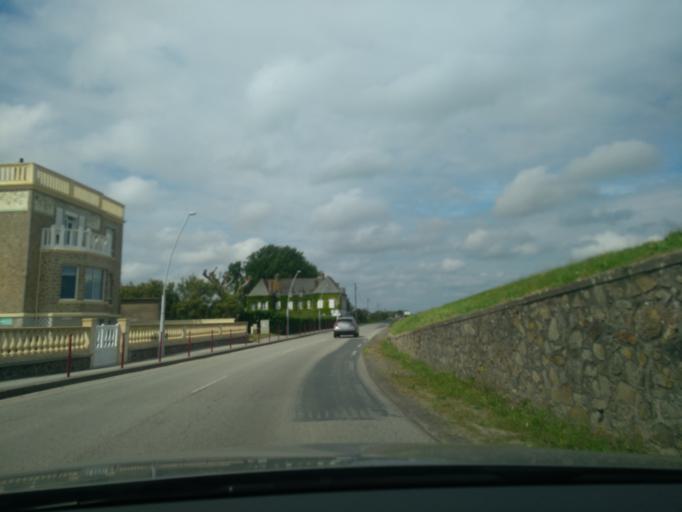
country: FR
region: Lower Normandy
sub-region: Departement de la Manche
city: Saint-Vaast-la-Hougue
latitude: 49.5928
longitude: -1.2668
